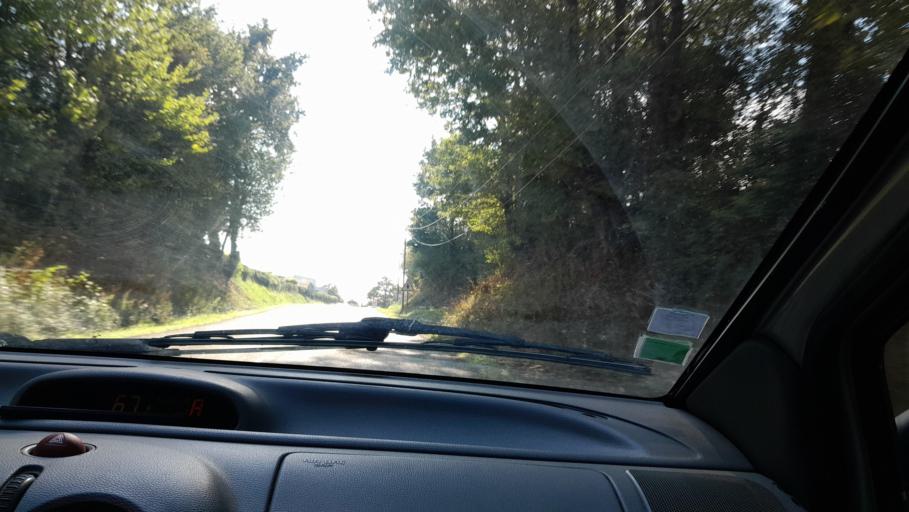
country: FR
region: Pays de la Loire
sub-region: Departement de la Mayenne
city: Ahuille
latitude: 48.0236
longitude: -0.8629
